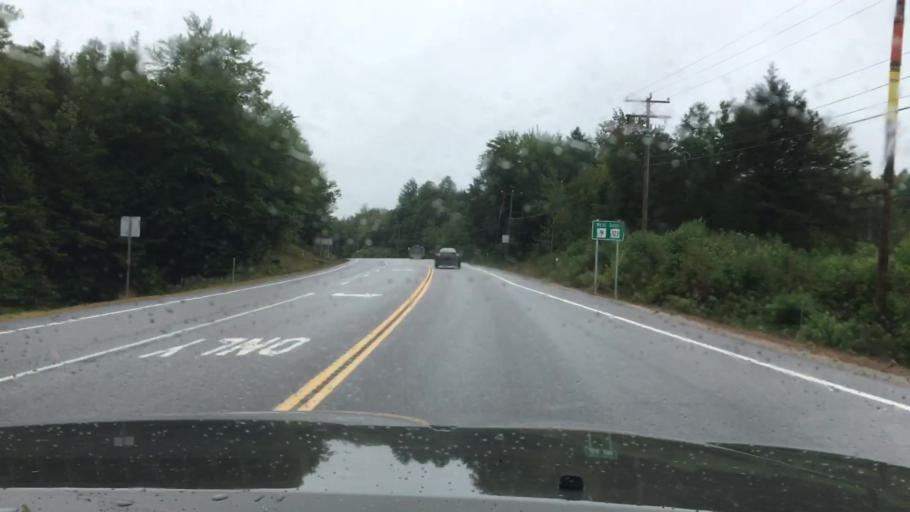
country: US
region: New Hampshire
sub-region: Cheshire County
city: Harrisville
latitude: 43.0567
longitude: -72.0777
